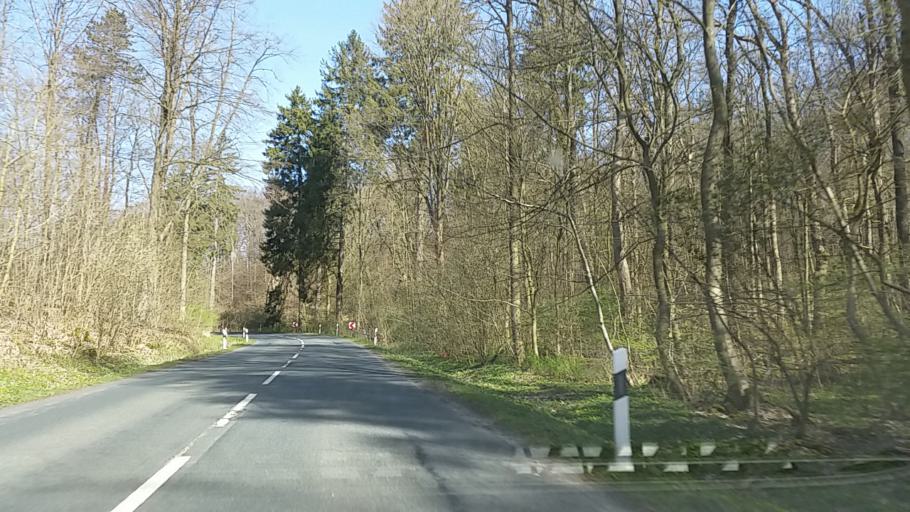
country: DE
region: Lower Saxony
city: Konigslutter am Elm
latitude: 52.2111
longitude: 10.8025
